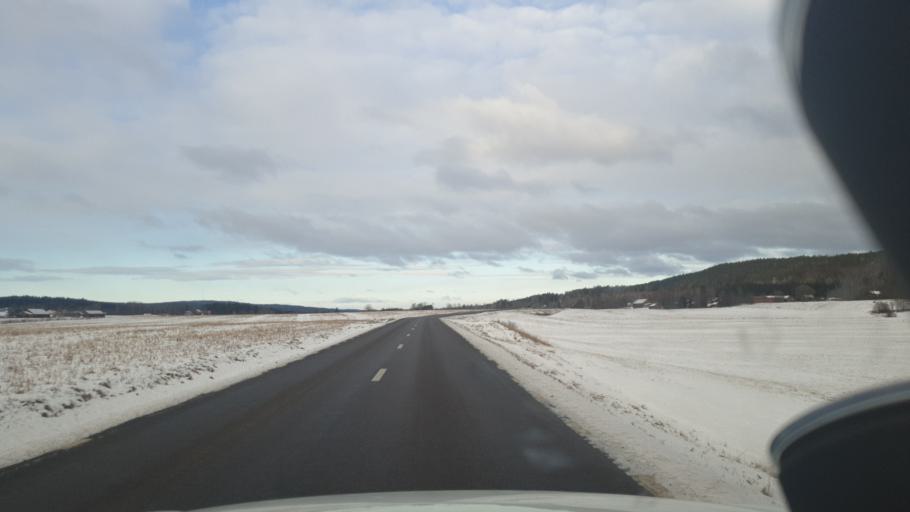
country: SE
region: Vaermland
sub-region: Eda Kommun
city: Amotfors
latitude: 59.6555
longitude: 12.1411
